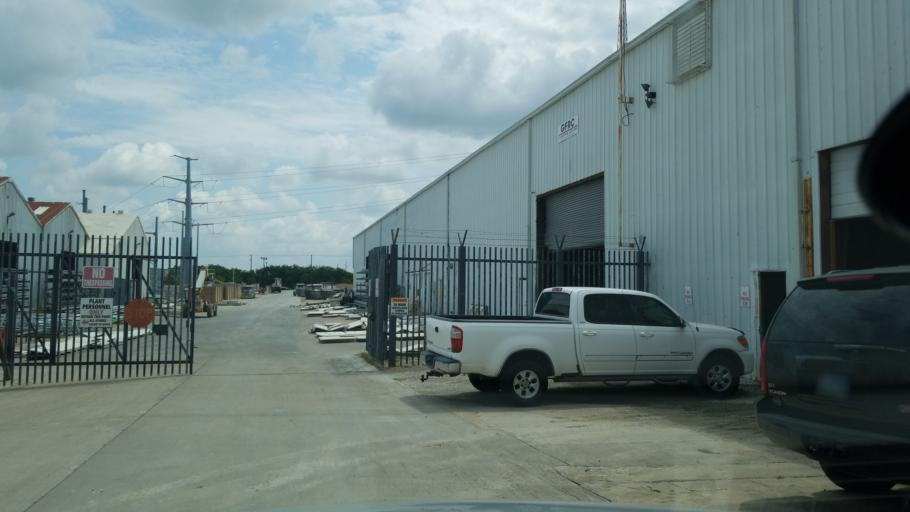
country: US
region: Texas
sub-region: Dallas County
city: Garland
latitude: 32.9131
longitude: -96.6634
